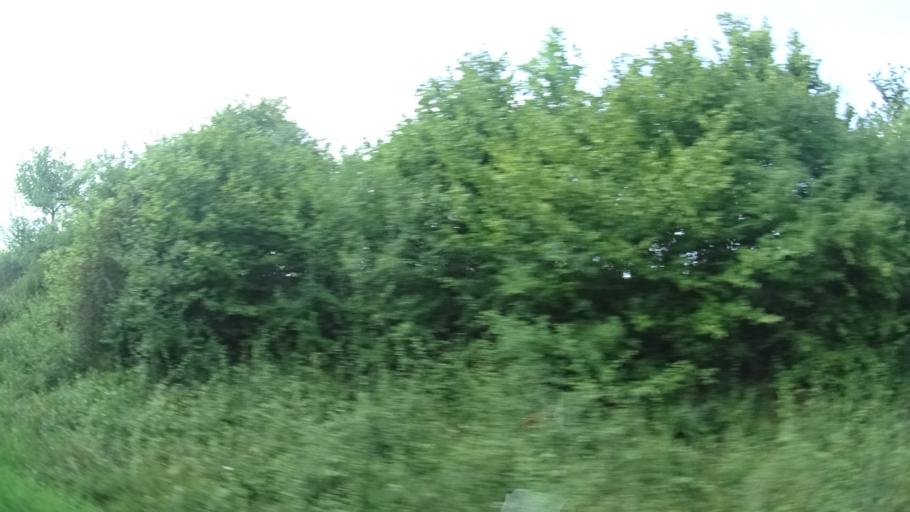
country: DE
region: Bavaria
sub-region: Regierungsbezirk Unterfranken
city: Bergrheinfeld
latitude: 49.9966
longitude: 10.1582
